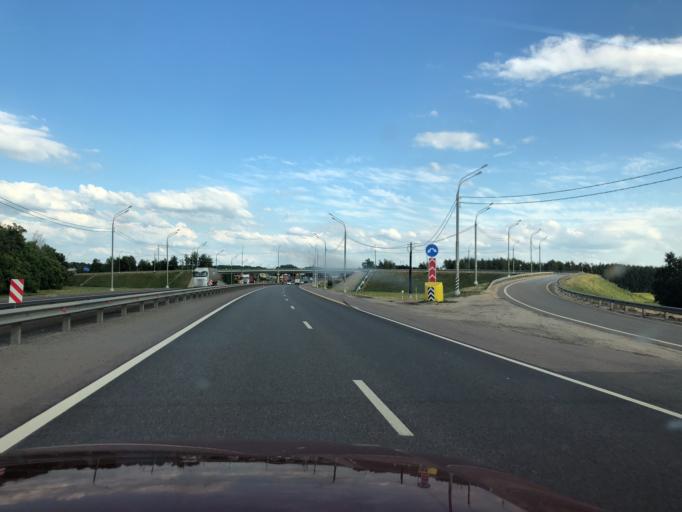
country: RU
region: Lipetsk
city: Zadonsk
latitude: 52.4374
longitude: 38.8128
